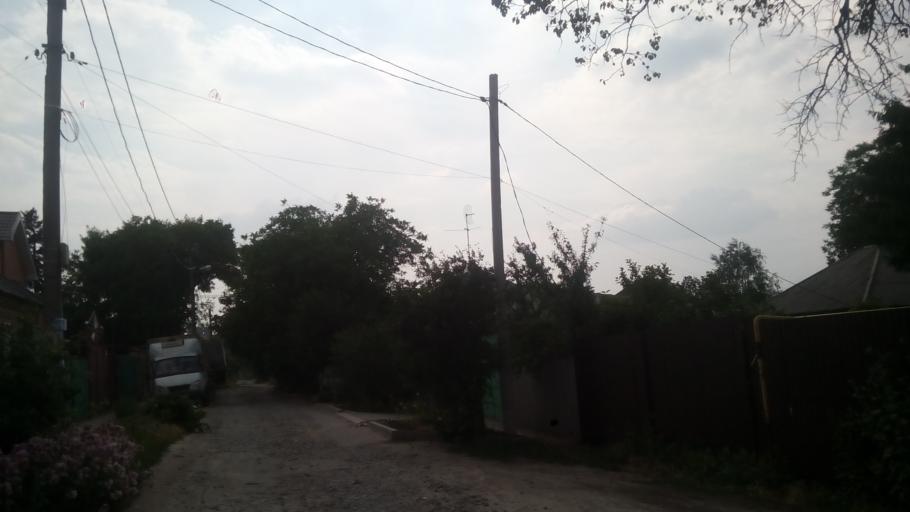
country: RU
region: Rostov
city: Rostov-na-Donu
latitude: 47.2202
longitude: 39.6416
